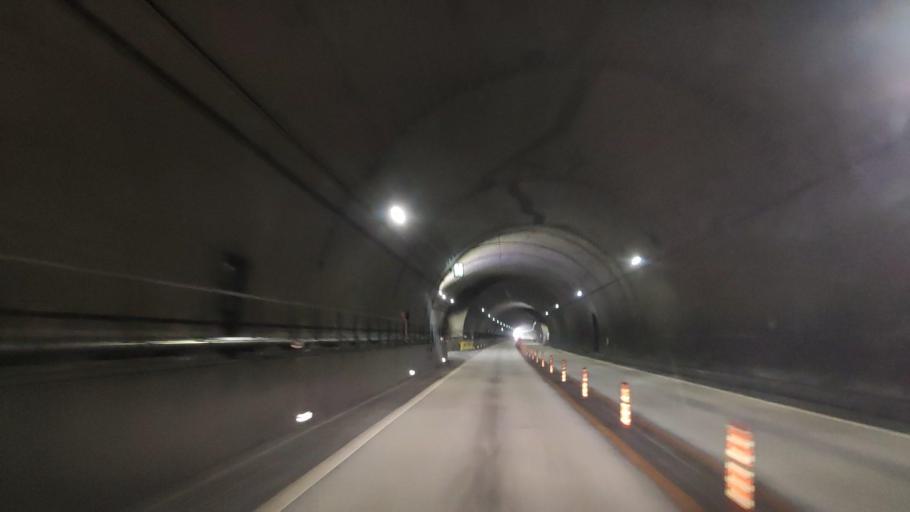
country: JP
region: Ehime
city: Hojo
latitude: 34.0828
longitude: 132.9772
